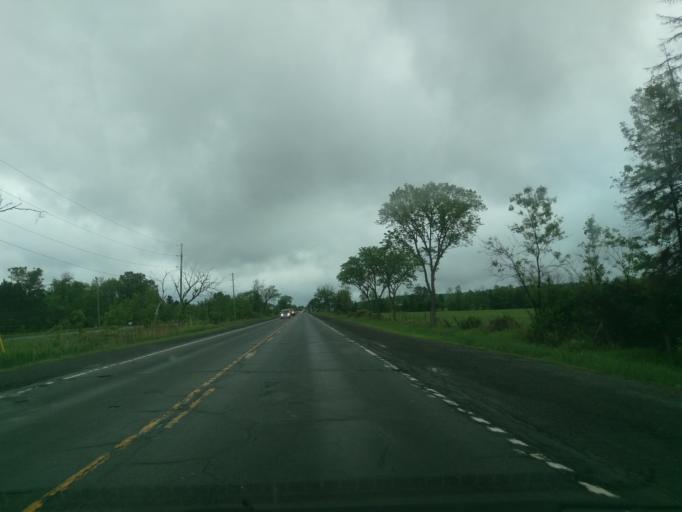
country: CA
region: Ontario
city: Clarence-Rockland
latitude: 45.5224
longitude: -75.3455
